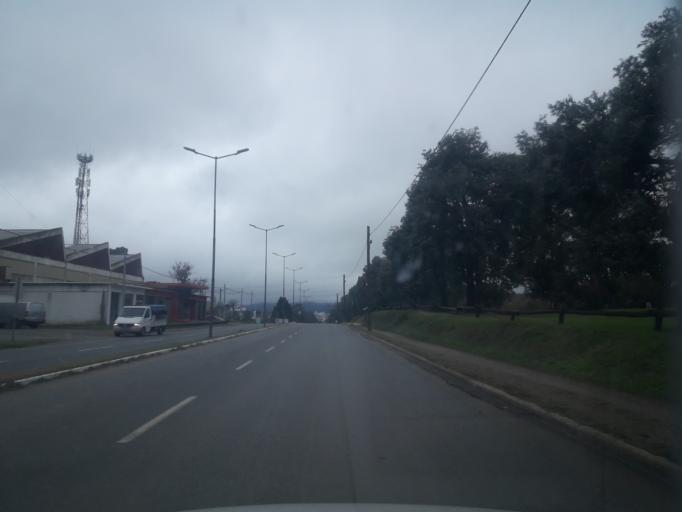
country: AR
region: Buenos Aires
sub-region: Partido de Tandil
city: Tandil
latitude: -37.3025
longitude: -59.1680
